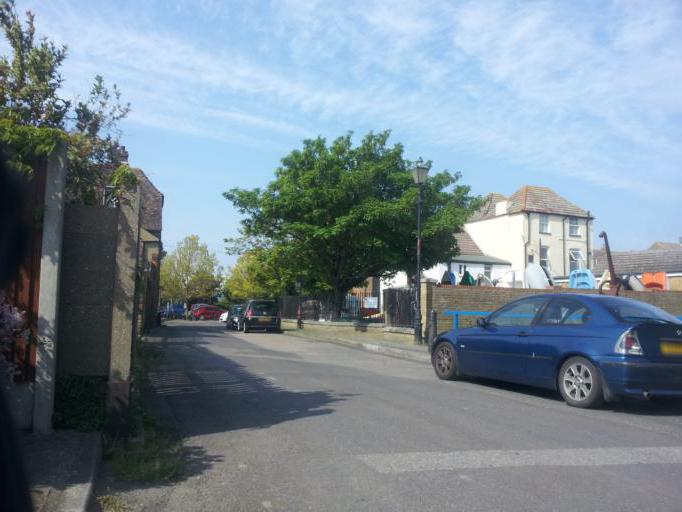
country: GB
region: England
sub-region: Kent
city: Queenborough
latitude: 51.4165
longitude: 0.7412
